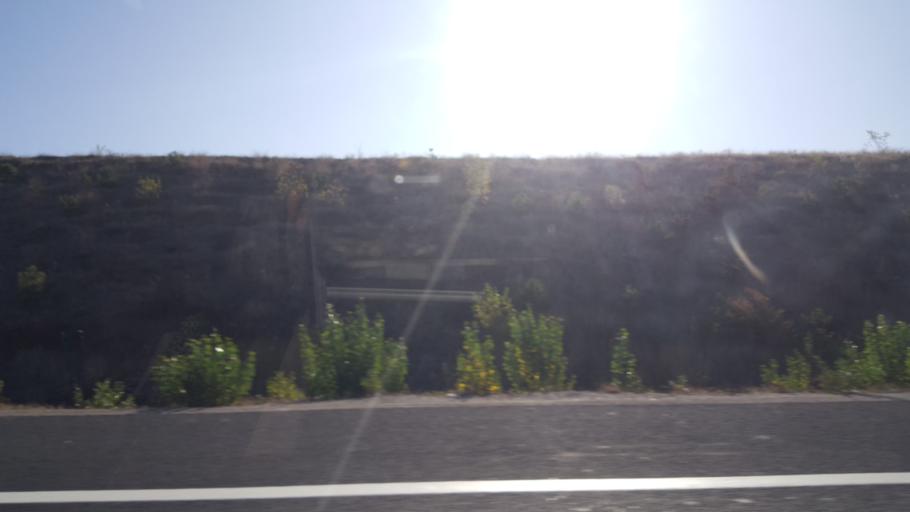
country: TR
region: Ankara
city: Mamak
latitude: 39.9064
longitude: 32.9986
